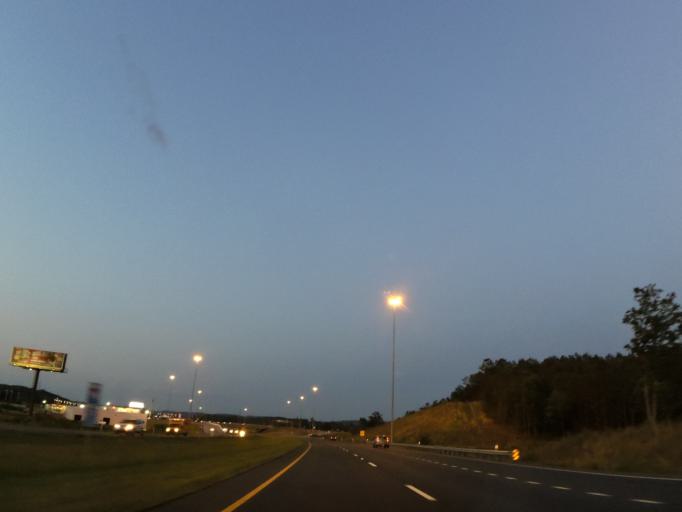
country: US
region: Tennessee
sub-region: Bradley County
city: Cleveland
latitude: 35.1494
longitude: -84.9534
